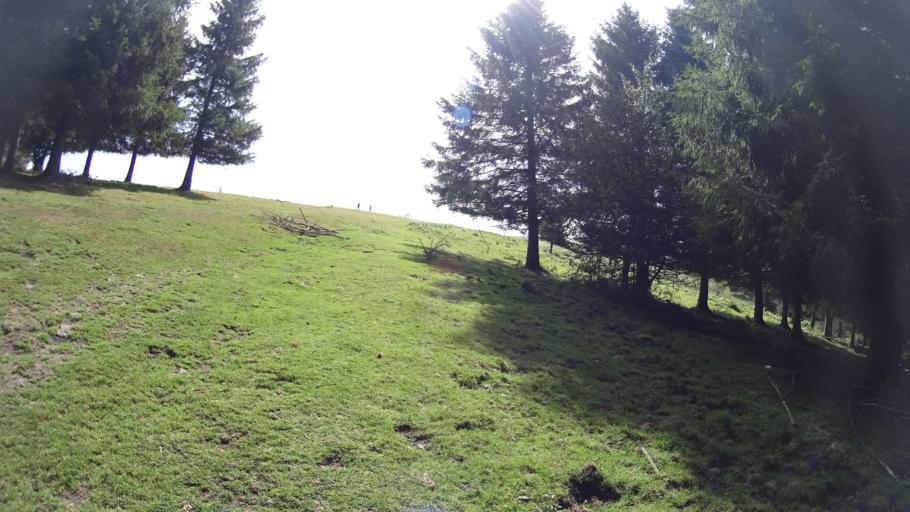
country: ES
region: Basque Country
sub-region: Bizkaia
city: Manaria
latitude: 43.0973
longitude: -2.6341
